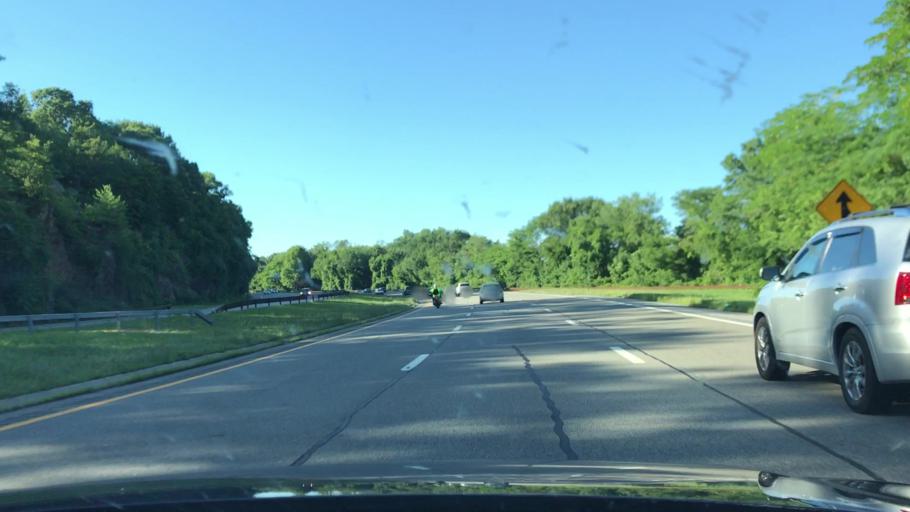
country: US
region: New York
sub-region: Westchester County
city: Yorktown Heights
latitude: 41.2684
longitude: -73.8070
